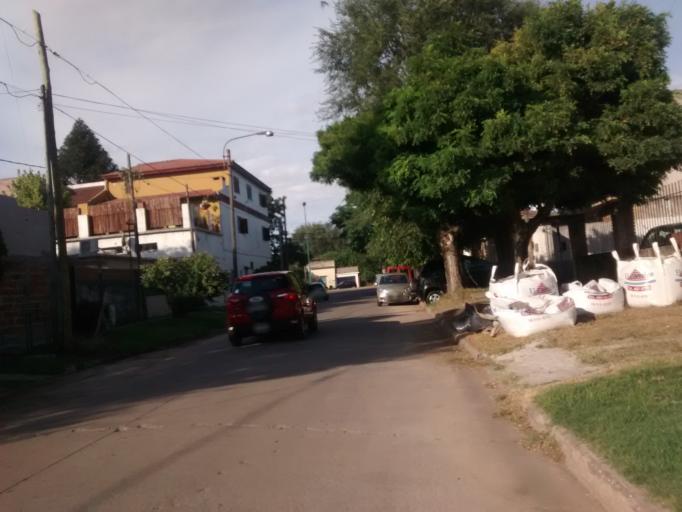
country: AR
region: Buenos Aires
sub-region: Partido de La Plata
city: La Plata
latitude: -34.8551
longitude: -58.0778
